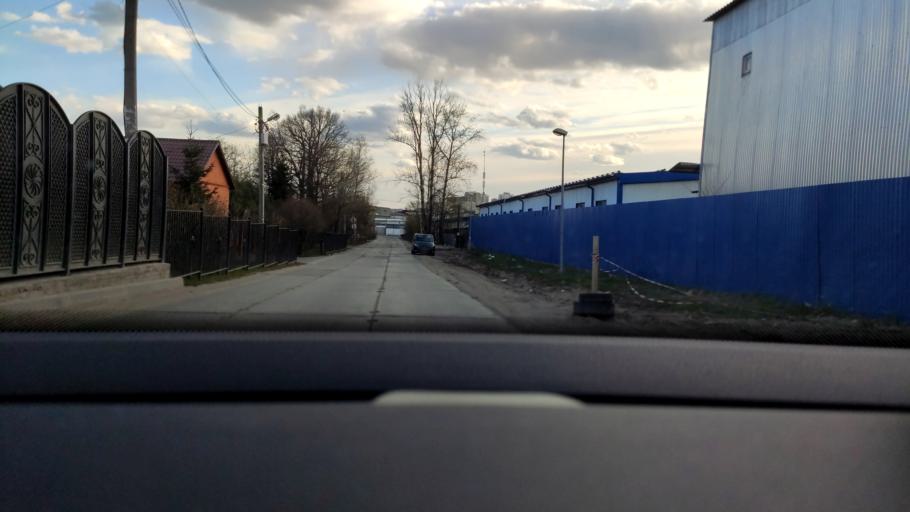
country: RU
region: Moskovskaya
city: Reutov
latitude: 55.7730
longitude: 37.8844
